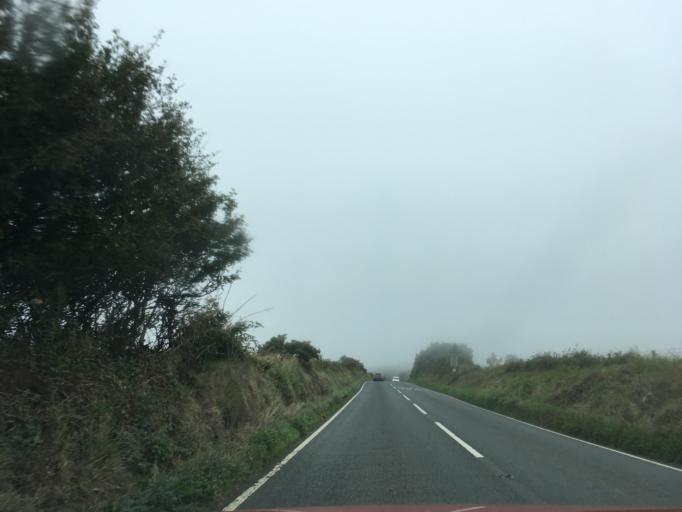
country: GB
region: Wales
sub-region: Pembrokeshire
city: Saint David's
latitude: 51.8776
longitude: -5.2114
